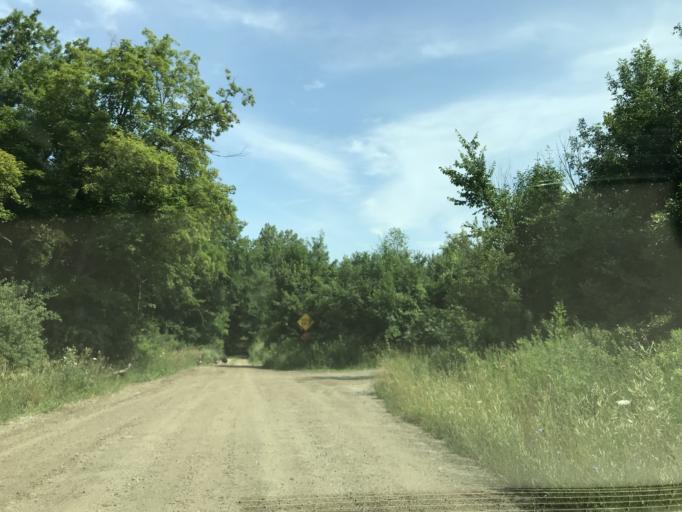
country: US
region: Michigan
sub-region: Eaton County
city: Grand Ledge
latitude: 42.7783
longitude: -84.7198
